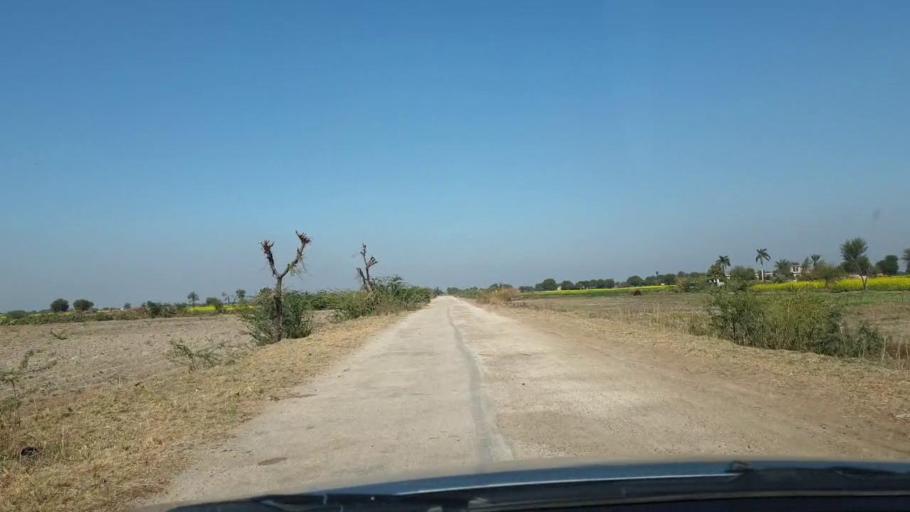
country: PK
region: Sindh
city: Jhol
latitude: 25.9231
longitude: 68.9080
